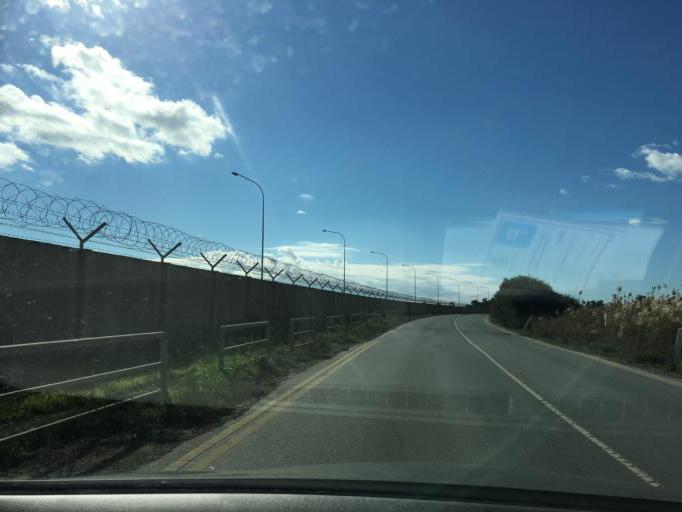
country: CY
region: Limassol
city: Limassol
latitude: 34.6486
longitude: 33.0065
